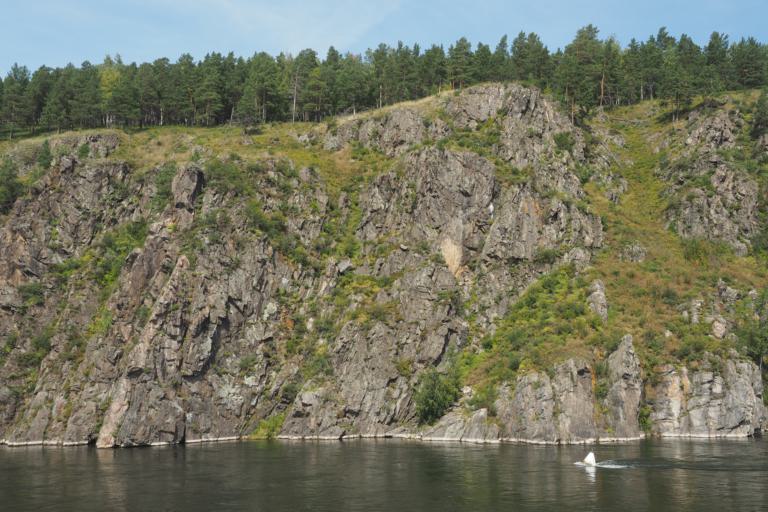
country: RU
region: Krasnoyarskiy
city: Zheleznogorsk
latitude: 56.3818
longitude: 93.5979
